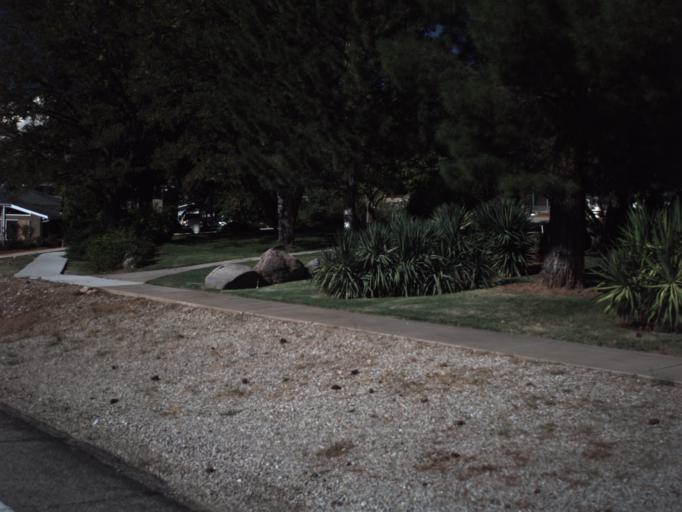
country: US
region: Utah
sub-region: Washington County
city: Toquerville
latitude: 37.2562
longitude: -113.2855
